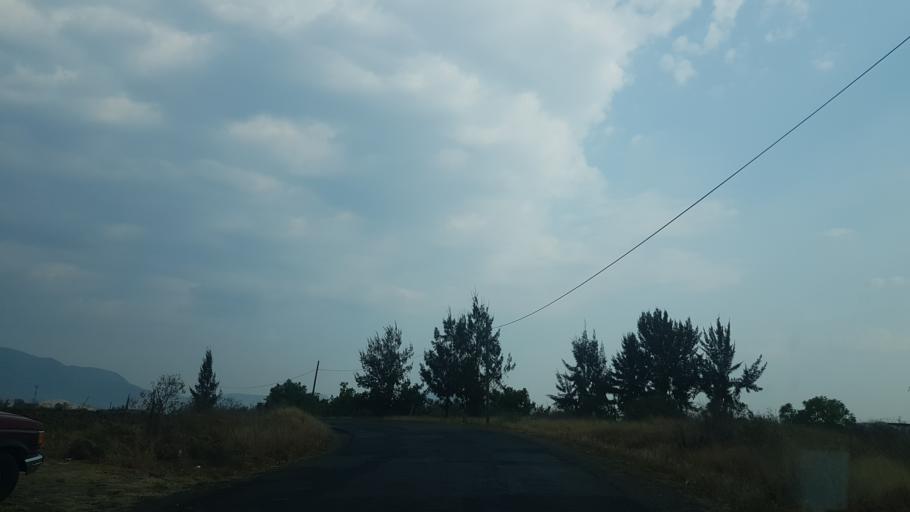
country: MX
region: Puebla
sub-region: Santa Isabel Cholula
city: Santa Ana Acozautla
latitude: 18.9587
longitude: -98.3949
